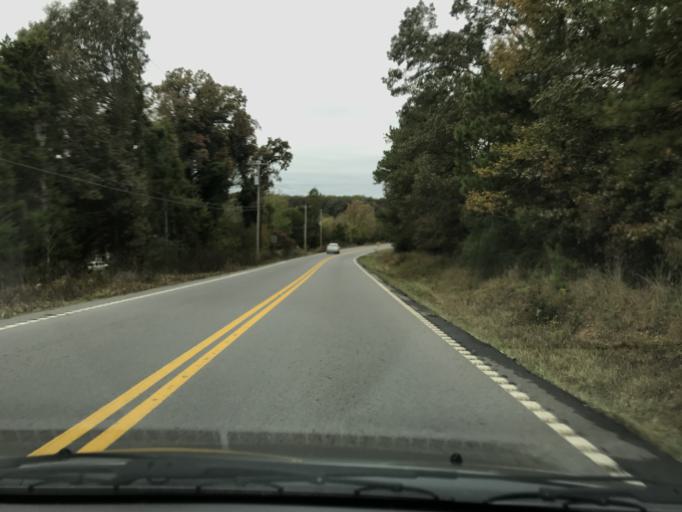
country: US
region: Tennessee
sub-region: Hamilton County
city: Sale Creek
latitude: 35.3516
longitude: -84.9896
